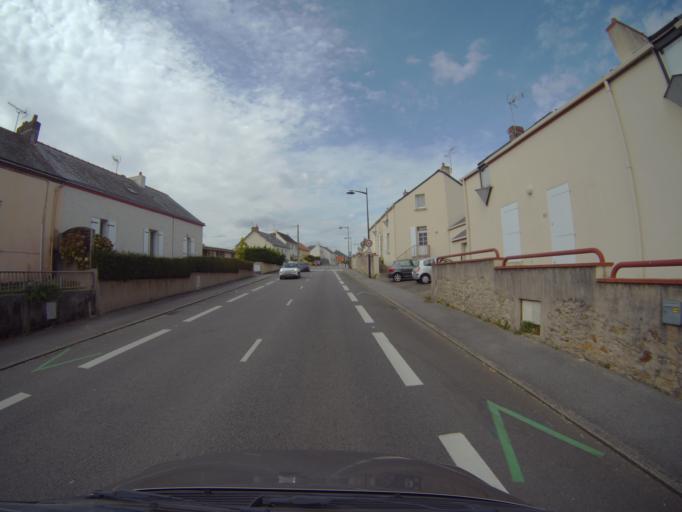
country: FR
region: Pays de la Loire
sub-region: Departement de la Loire-Atlantique
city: Saint-Herblain
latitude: 47.2085
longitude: -1.6393
